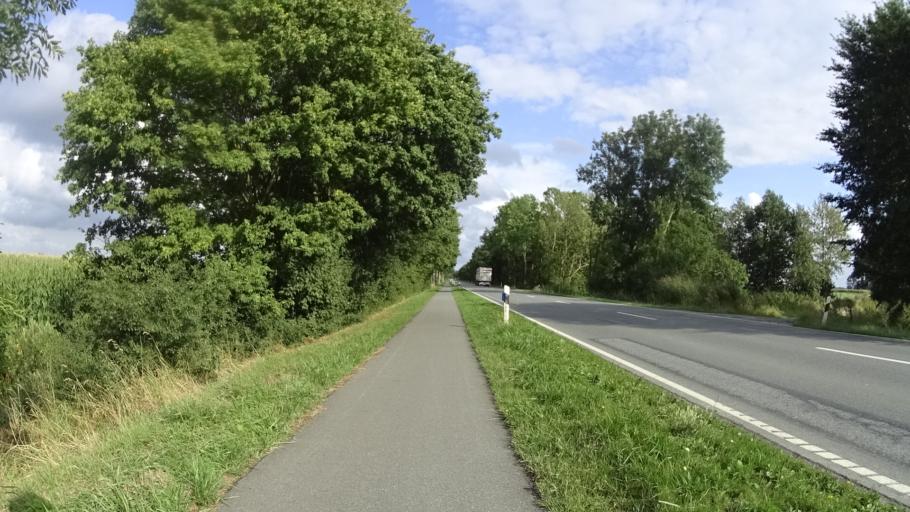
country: DE
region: Lower Saxony
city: Varel
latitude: 53.3911
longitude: 8.1884
